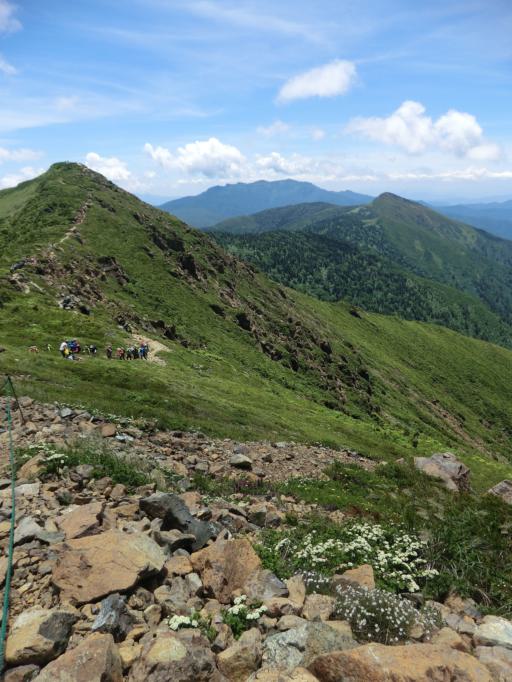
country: JP
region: Gunma
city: Numata
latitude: 36.8994
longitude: 139.1712
